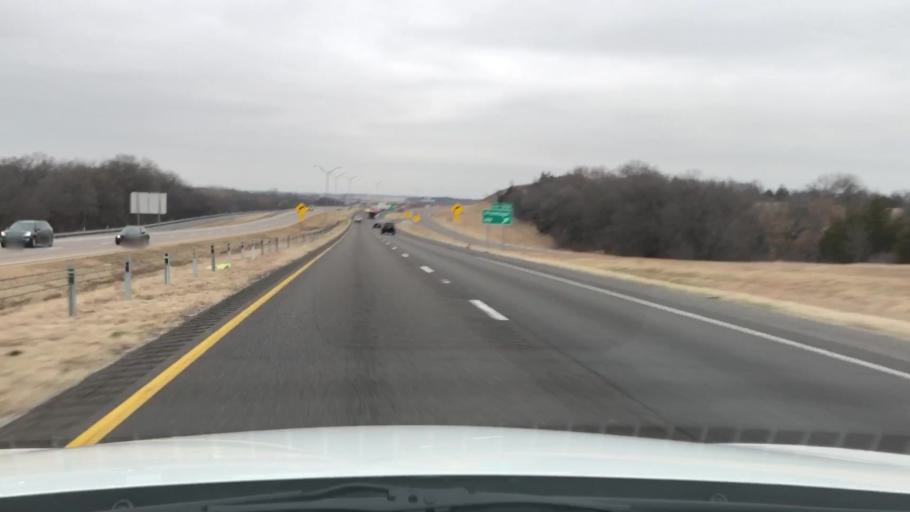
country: US
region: Texas
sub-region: Cooke County
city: Gainesville
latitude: 33.7206
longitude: -97.1611
